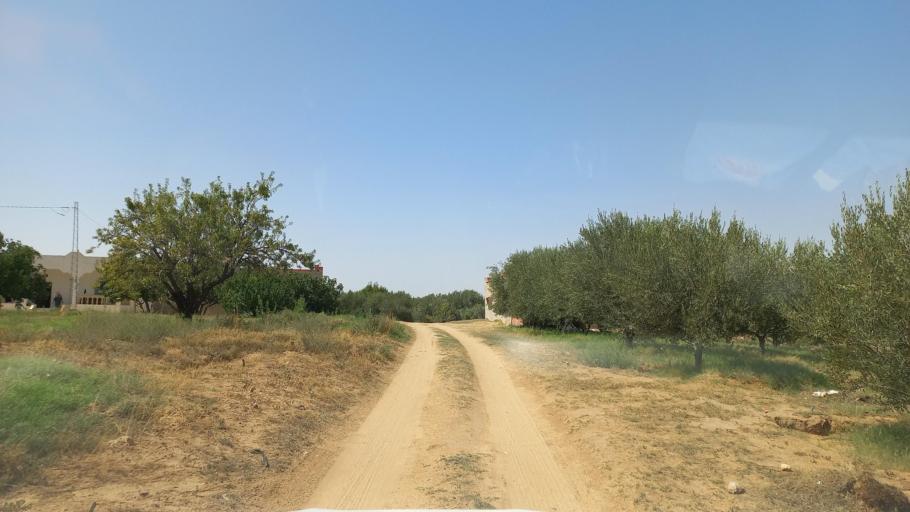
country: TN
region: Al Qasrayn
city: Kasserine
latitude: 35.2365
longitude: 9.0291
